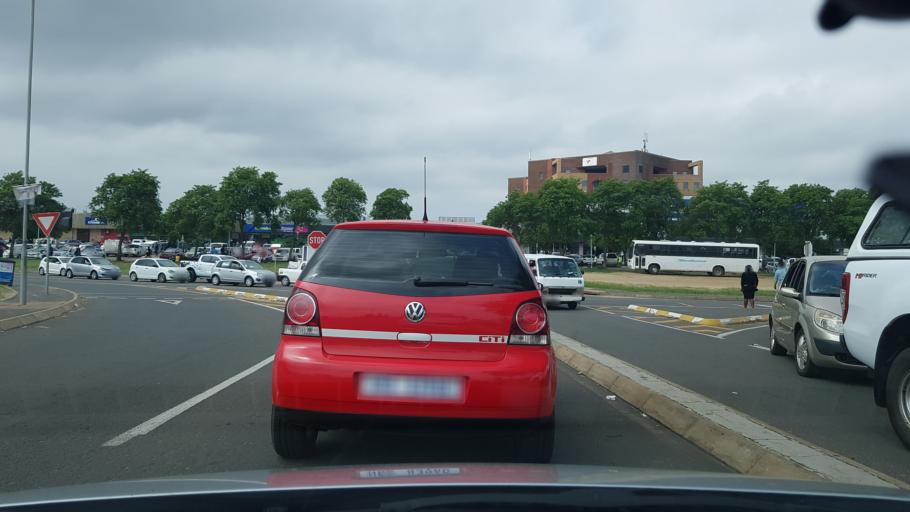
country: ZA
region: KwaZulu-Natal
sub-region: uThungulu District Municipality
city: Richards Bay
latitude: -28.7542
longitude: 32.0481
